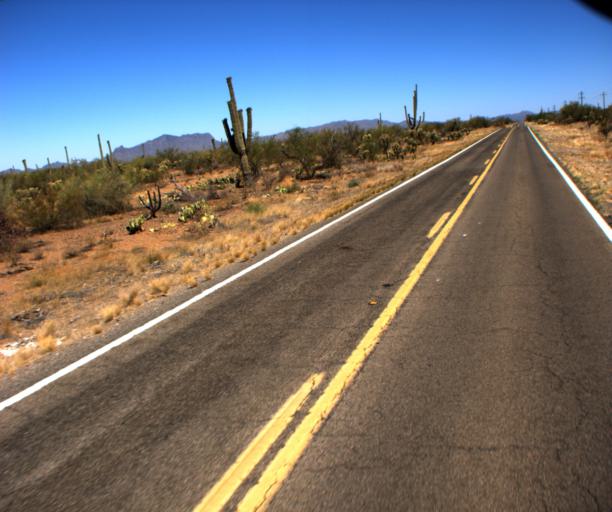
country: US
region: Arizona
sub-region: Pima County
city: Sells
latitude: 32.0046
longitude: -111.9889
